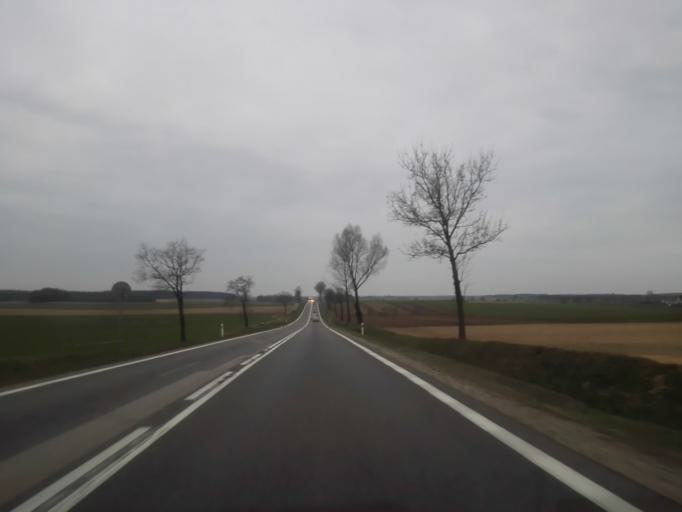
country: PL
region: Podlasie
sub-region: Powiat kolnenski
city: Stawiski
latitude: 53.4278
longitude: 22.1697
